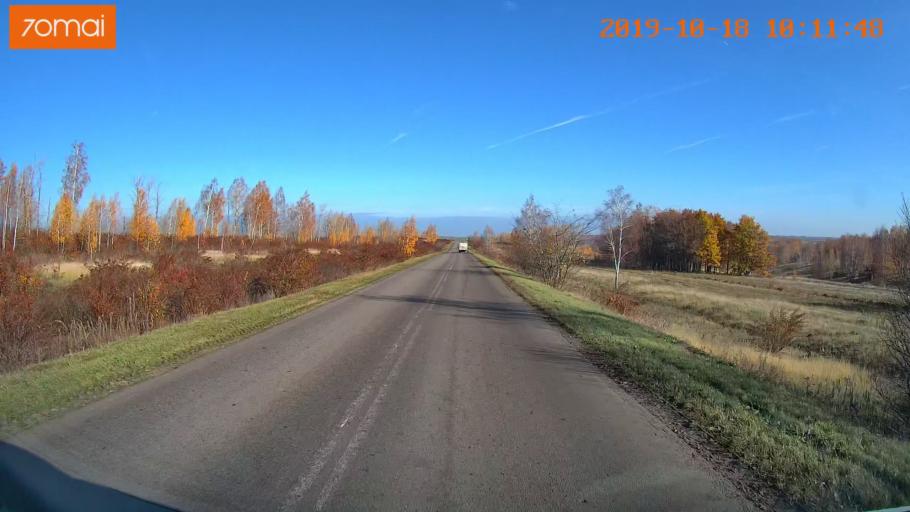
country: RU
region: Tula
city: Kurkino
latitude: 53.3862
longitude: 38.5028
